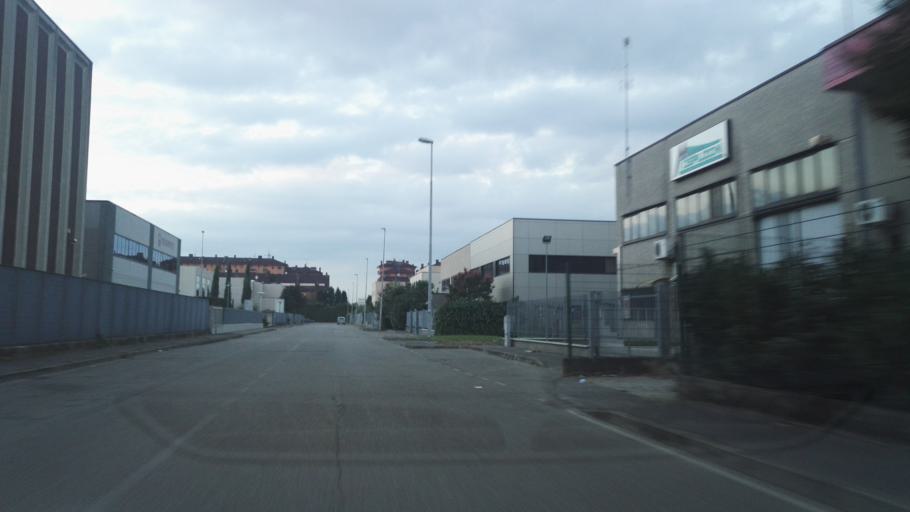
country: IT
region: Lombardy
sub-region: Citta metropolitana di Milano
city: San Giuliano Milanese
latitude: 45.3821
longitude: 9.3084
